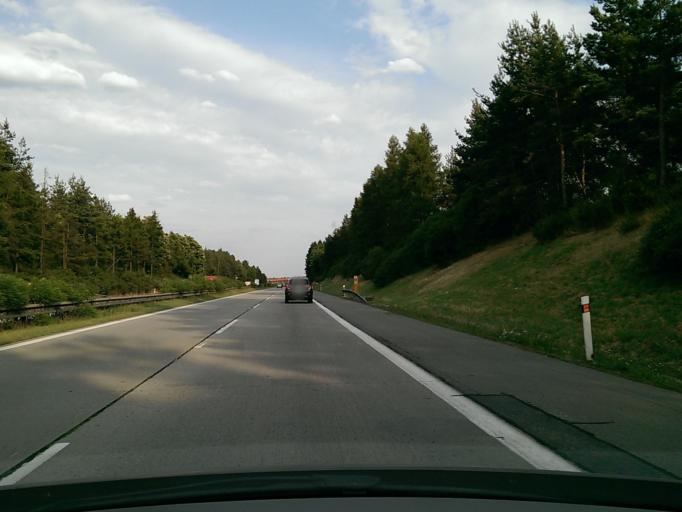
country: CZ
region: Vysocina
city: Dobronin
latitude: 49.4377
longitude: 15.6409
